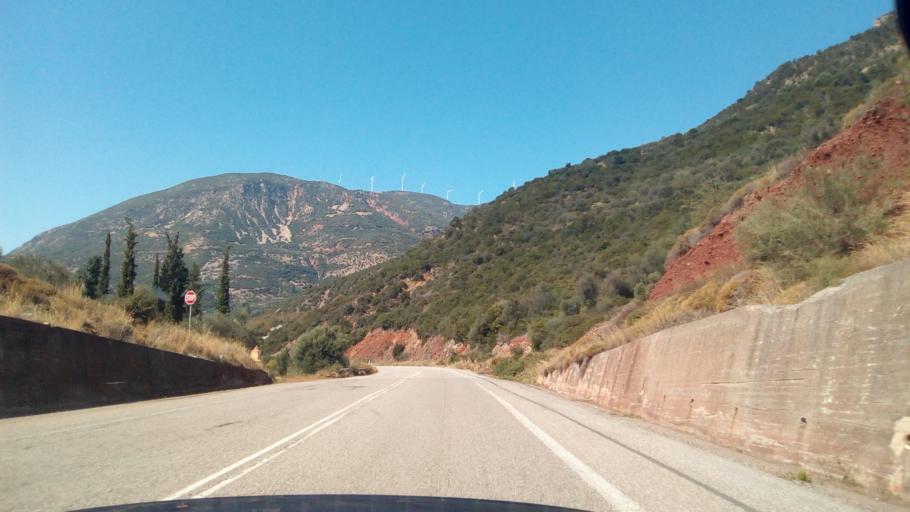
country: GR
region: West Greece
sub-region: Nomos Achaias
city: Selianitika
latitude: 38.3916
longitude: 22.0732
